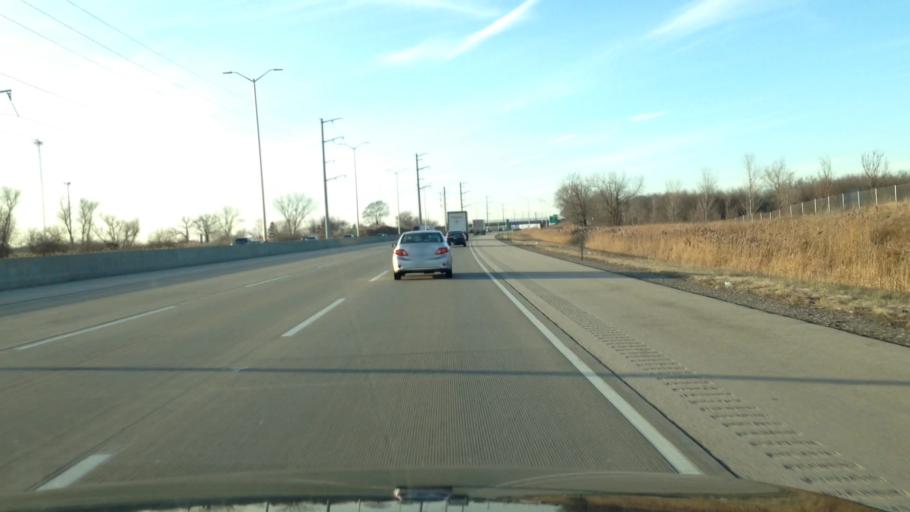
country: US
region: Illinois
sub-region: Kane County
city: Gilberts
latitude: 42.1076
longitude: -88.4007
